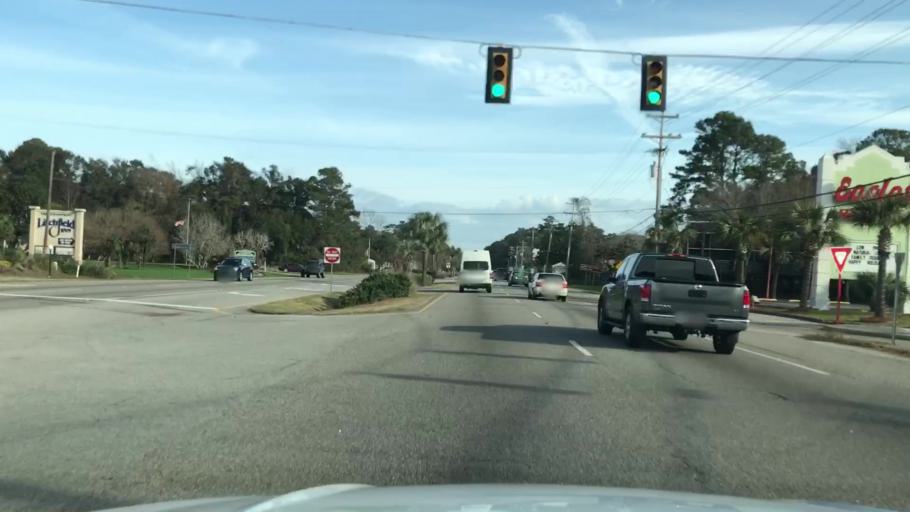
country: US
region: South Carolina
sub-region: Georgetown County
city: Murrells Inlet
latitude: 33.4718
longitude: -79.1048
